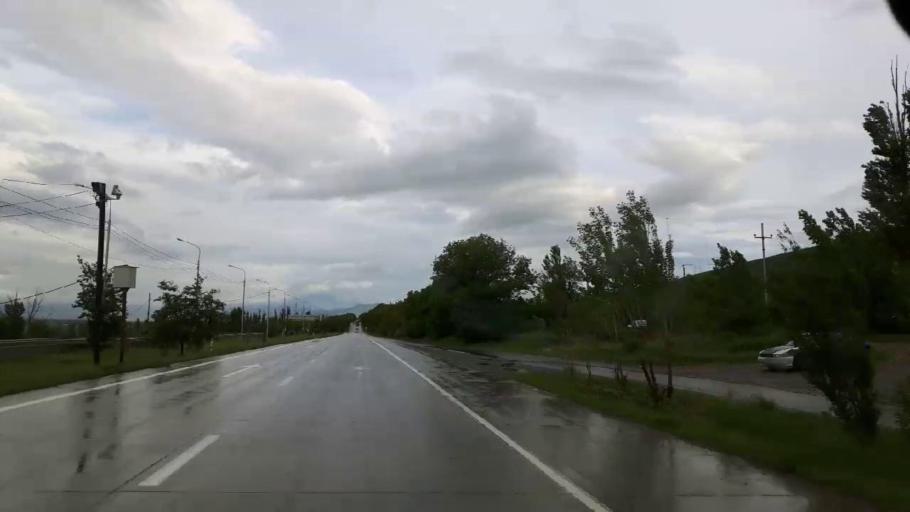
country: GE
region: Shida Kartli
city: Kaspi
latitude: 41.9622
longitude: 44.4748
